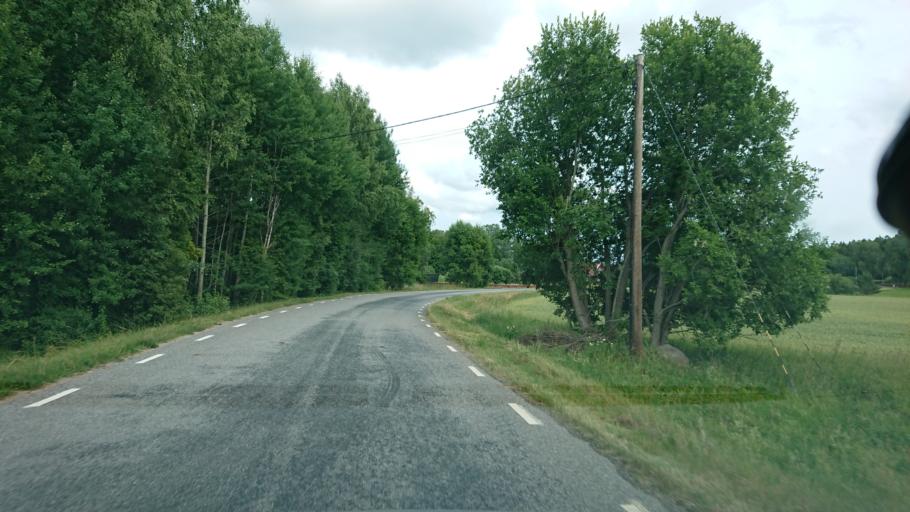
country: SE
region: Uppsala
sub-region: Osthammars Kommun
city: Bjorklinge
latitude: 60.0034
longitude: 17.4607
